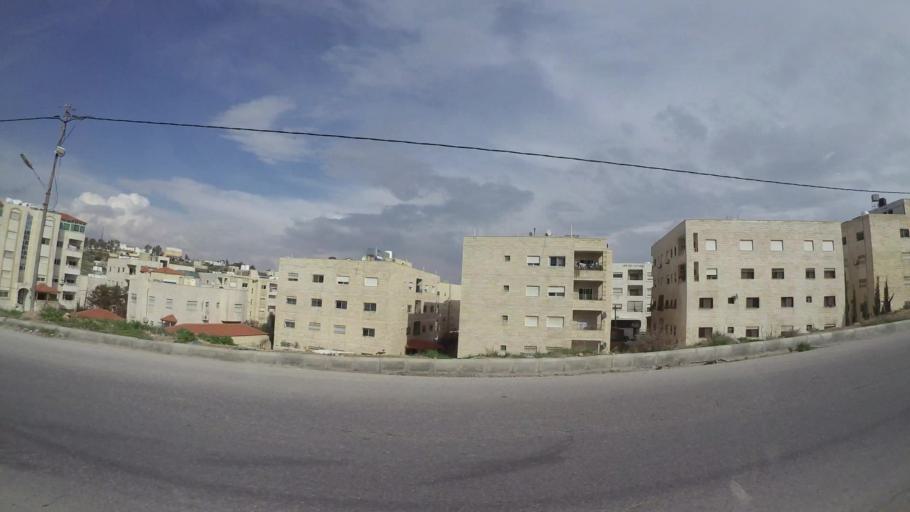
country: JO
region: Amman
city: Amman
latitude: 32.0106
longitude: 35.9523
